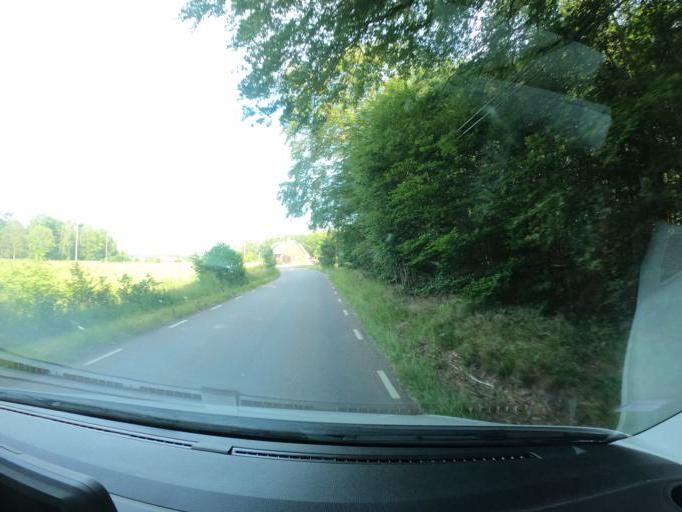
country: SE
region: Skane
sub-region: Angelholms Kommun
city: Munka-Ljungby
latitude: 56.3341
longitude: 12.9644
